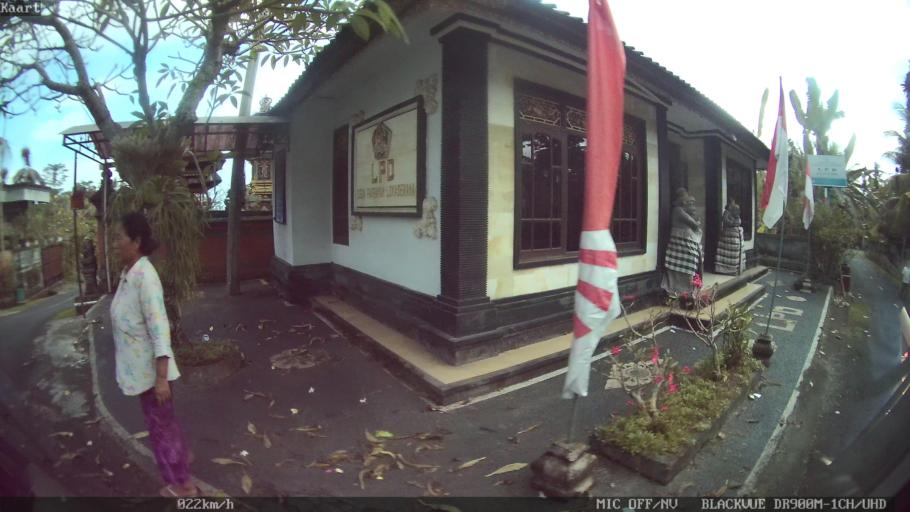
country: ID
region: Bali
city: Banjar Pesalakan
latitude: -8.5161
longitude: 115.3070
